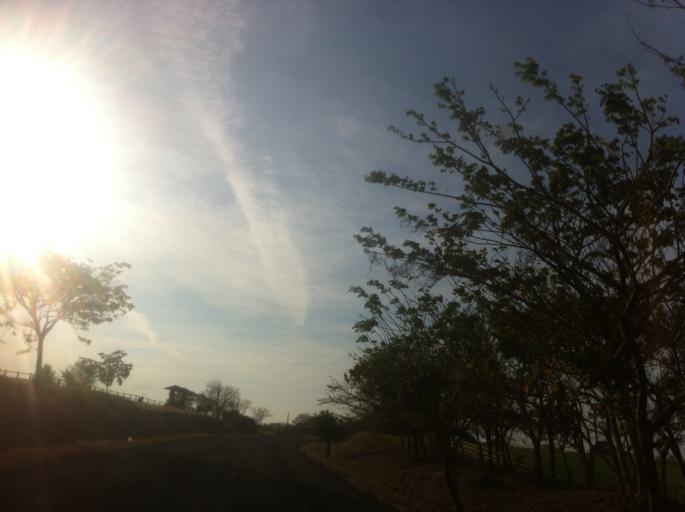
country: NI
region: Rivas
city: Cardenas
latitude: 11.2879
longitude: -85.6779
